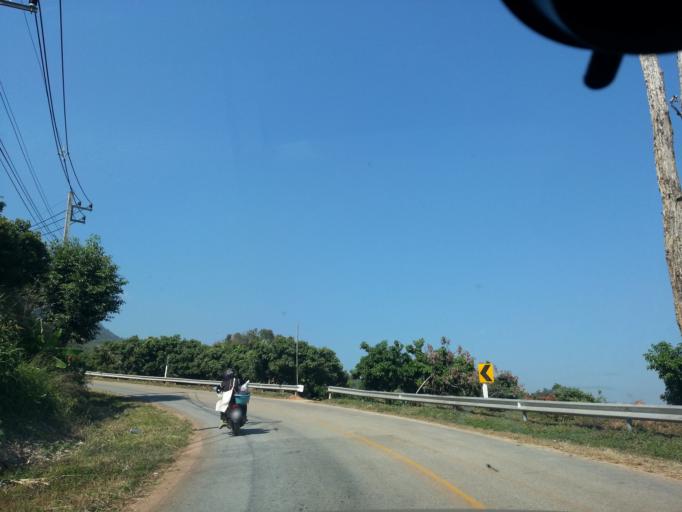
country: TH
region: Chiang Mai
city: Chai Prakan
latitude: 19.8286
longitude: 99.1035
